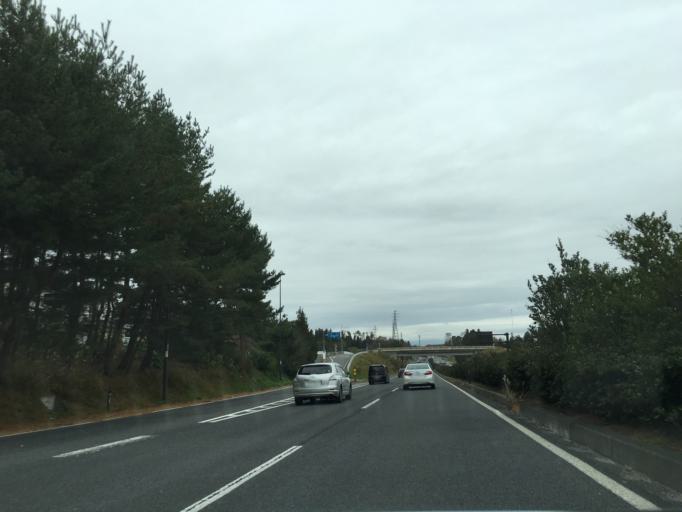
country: JP
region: Fukushima
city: Koriyama
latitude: 37.3462
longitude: 140.3571
